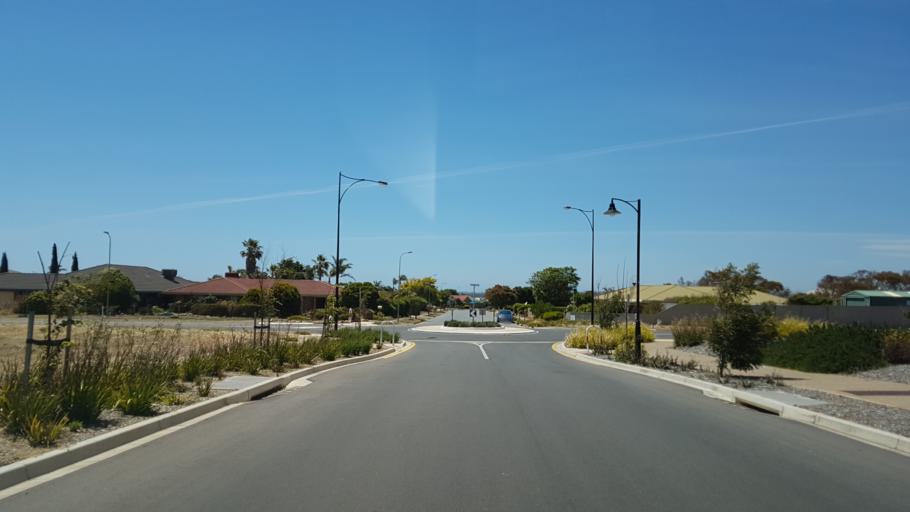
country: AU
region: South Australia
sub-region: Onkaparinga
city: Moana
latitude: -35.2168
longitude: 138.4751
